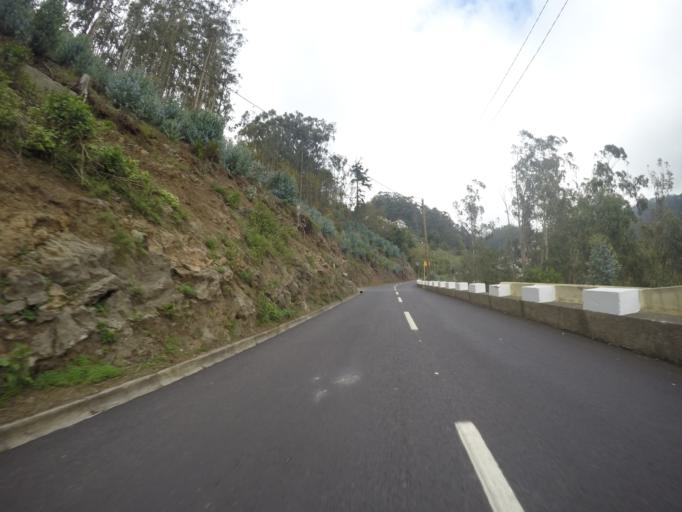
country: PT
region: Madeira
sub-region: Camara de Lobos
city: Curral das Freiras
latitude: 32.6844
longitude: -16.9539
